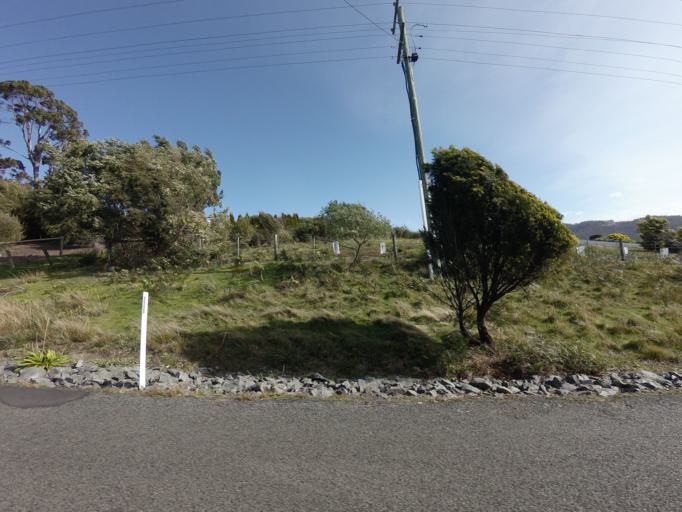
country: AU
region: Tasmania
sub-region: Kingborough
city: Margate
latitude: -43.0760
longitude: 147.2653
